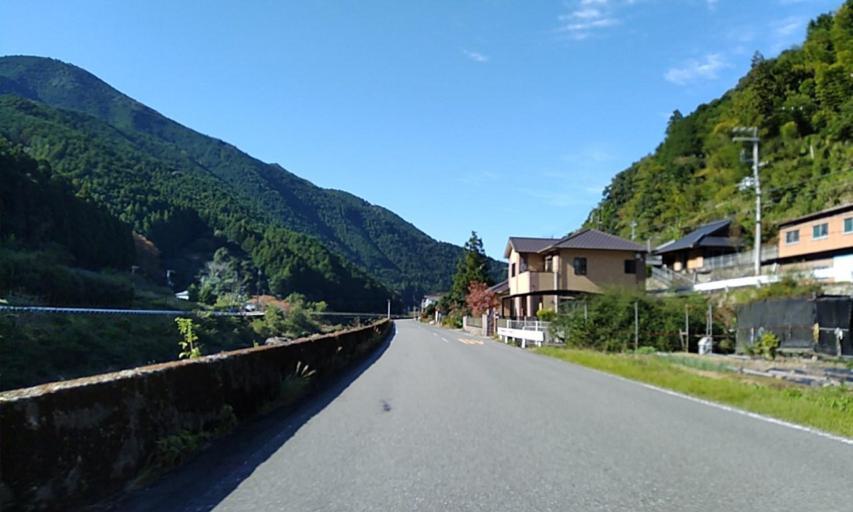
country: JP
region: Wakayama
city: Kainan
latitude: 34.0494
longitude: 135.3493
